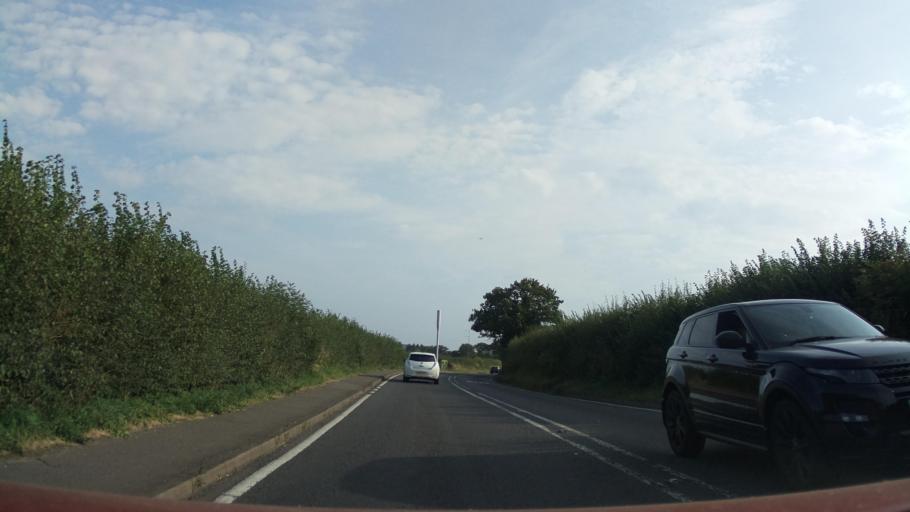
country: GB
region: England
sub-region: Warwickshire
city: Alcester
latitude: 52.2392
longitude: -1.8835
